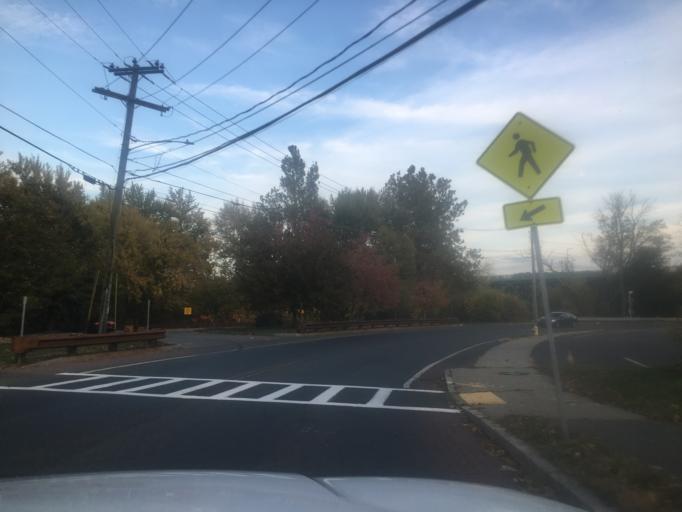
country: US
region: Massachusetts
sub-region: Hampden County
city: Springfield
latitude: 42.0821
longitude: -72.5864
